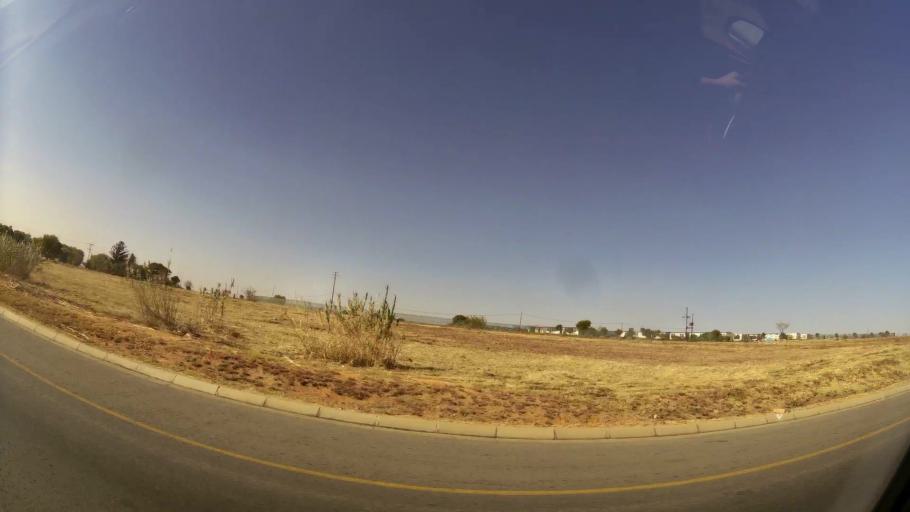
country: ZA
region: Gauteng
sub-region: West Rand District Municipality
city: Muldersdriseloop
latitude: -25.9921
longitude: 27.9248
